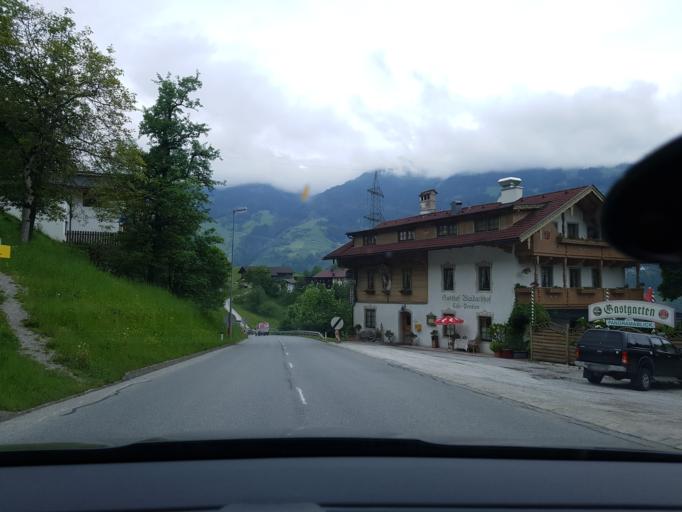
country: AT
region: Tyrol
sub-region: Politischer Bezirk Schwaz
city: Hainzenberg
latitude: 47.2221
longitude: 11.8908
